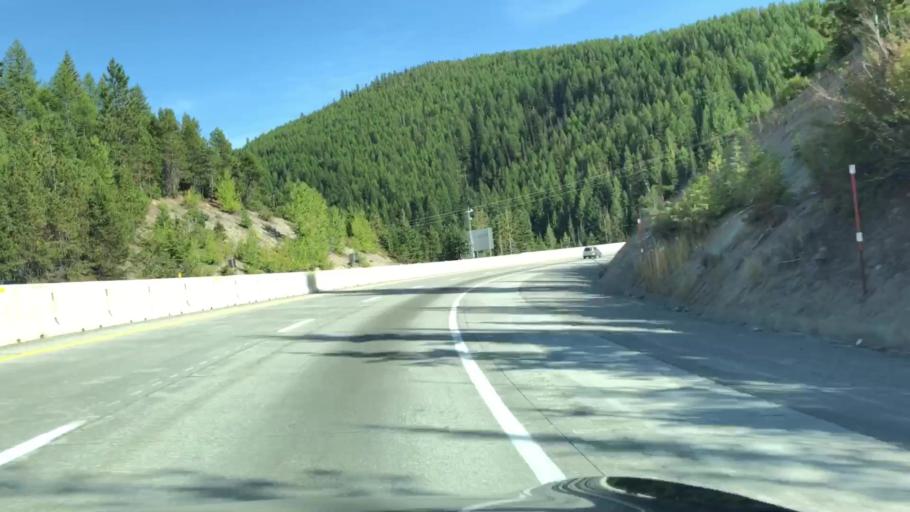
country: US
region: Idaho
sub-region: Shoshone County
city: Wallace
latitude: 47.4623
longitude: -115.6958
